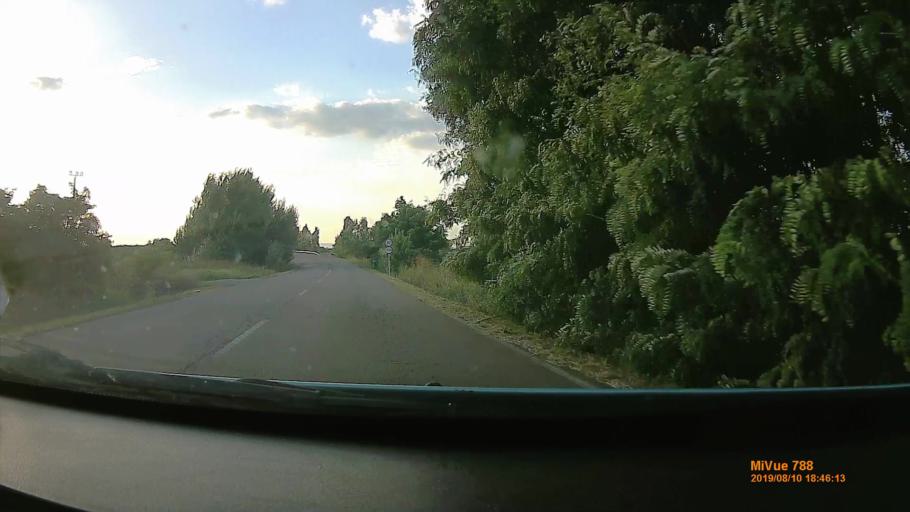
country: HU
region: Borsod-Abauj-Zemplen
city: Mezokovesd
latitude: 47.7744
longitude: 20.5890
